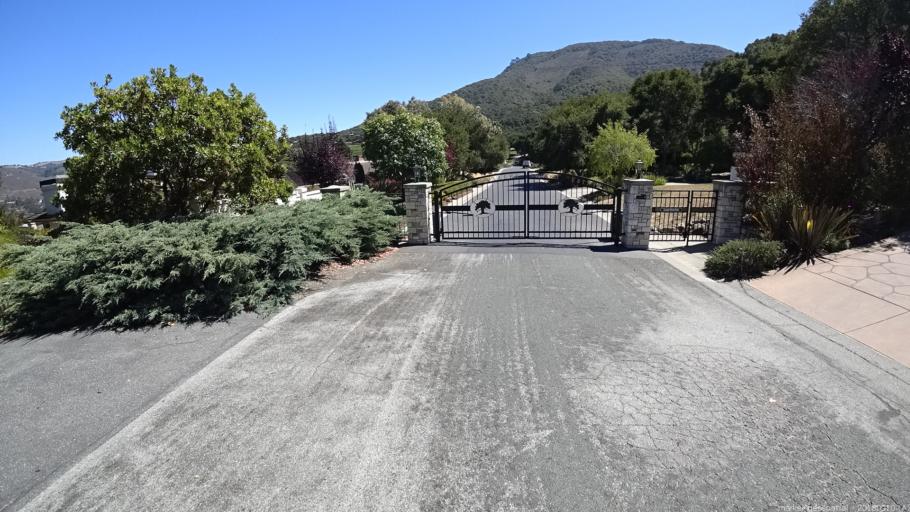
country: US
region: California
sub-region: Monterey County
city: Carmel Valley Village
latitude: 36.5148
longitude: -121.8026
